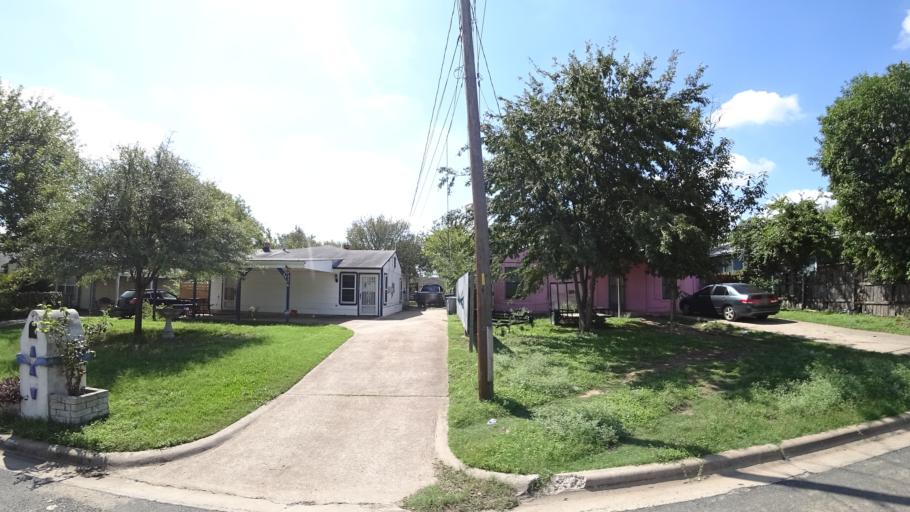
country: US
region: Texas
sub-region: Travis County
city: Austin
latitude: 30.3379
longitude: -97.7057
